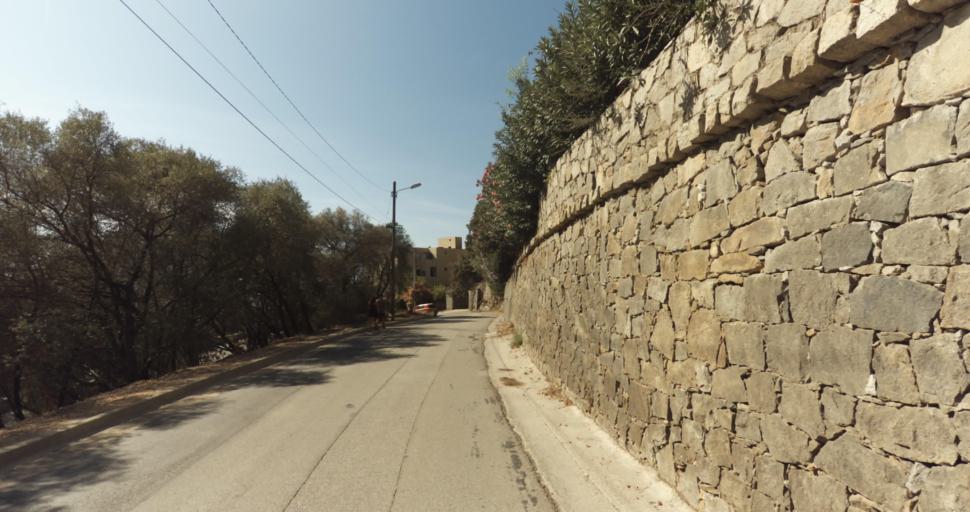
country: FR
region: Corsica
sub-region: Departement de la Corse-du-Sud
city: Ajaccio
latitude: 41.9229
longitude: 8.7295
